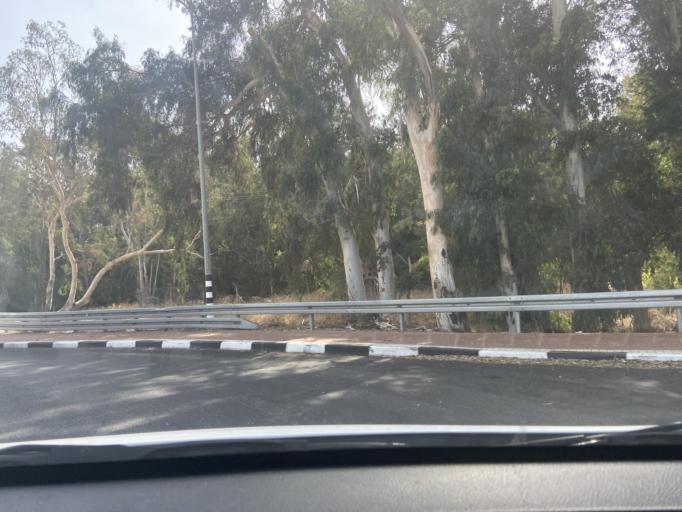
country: IL
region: Northern District
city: Nahariya
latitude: 33.0456
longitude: 35.1057
